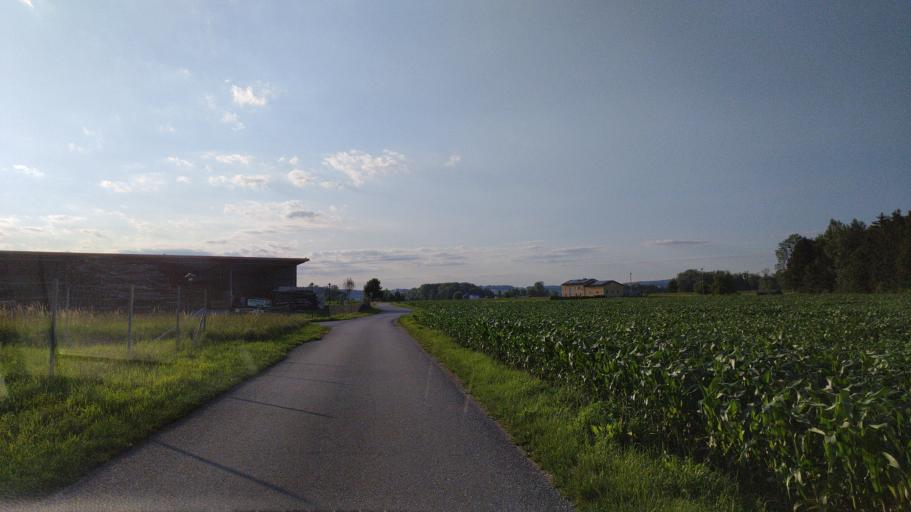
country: AT
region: Lower Austria
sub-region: Politischer Bezirk Amstetten
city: Ennsdorf
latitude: 48.2244
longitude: 14.5637
